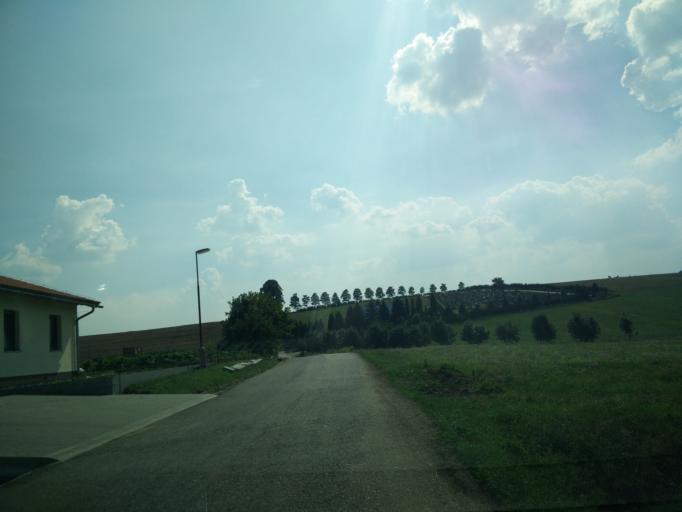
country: SK
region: Zilinsky
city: Rajec
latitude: 49.0608
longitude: 18.6521
